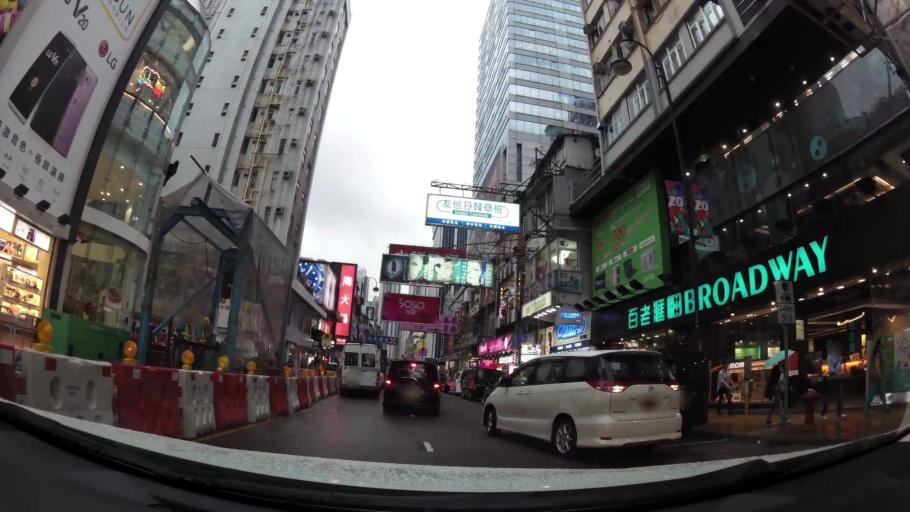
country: HK
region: Tsuen Wan
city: Tsuen Wan
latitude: 22.3704
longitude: 114.1174
